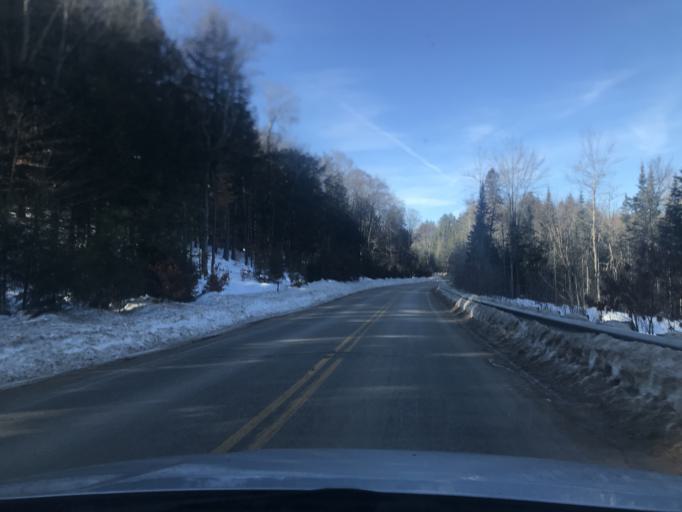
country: US
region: Michigan
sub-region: Dickinson County
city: Kingsford
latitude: 45.4104
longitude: -88.3609
